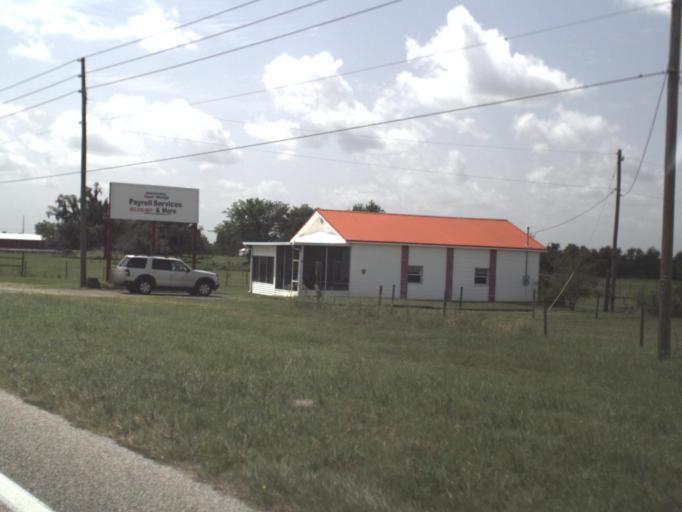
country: US
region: Florida
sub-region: Polk County
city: Lake Wales
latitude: 27.8834
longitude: -81.5991
